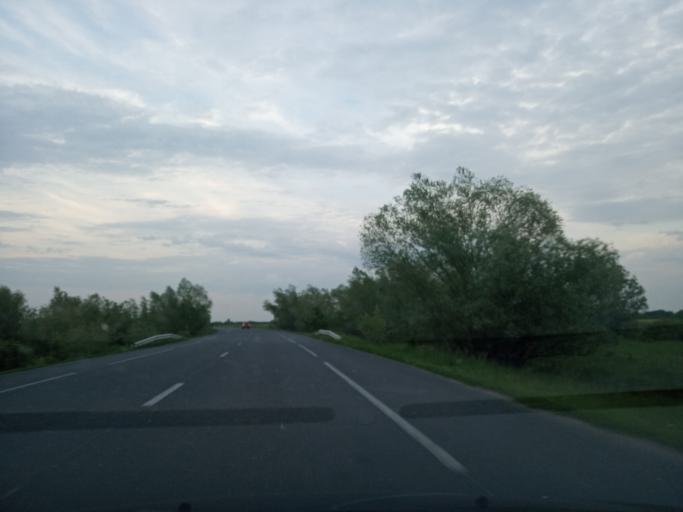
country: RO
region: Timis
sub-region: Oras Deta
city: Deta
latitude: 45.3960
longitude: 21.2363
